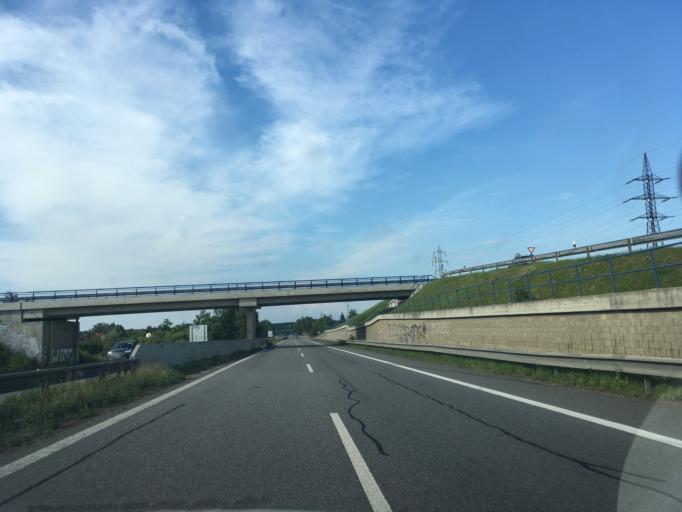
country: CZ
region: Vysocina
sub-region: Okres Jihlava
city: Jihlava
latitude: 49.4353
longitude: 15.5997
